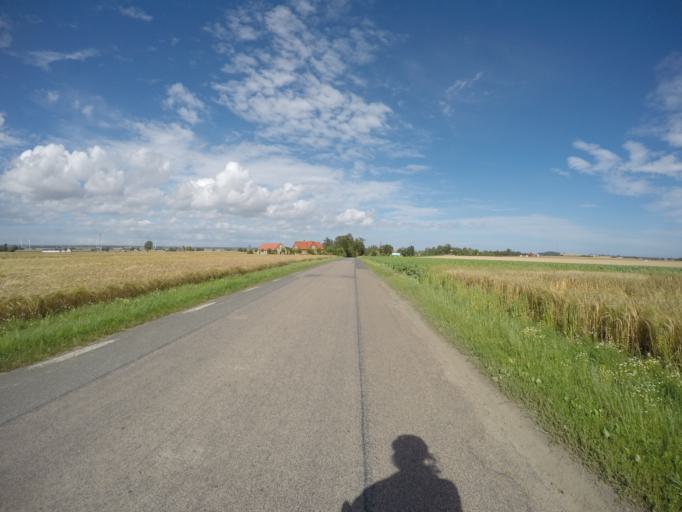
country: SE
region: Skane
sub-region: Simrishamns Kommun
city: Simrishamn
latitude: 55.4934
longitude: 14.1979
